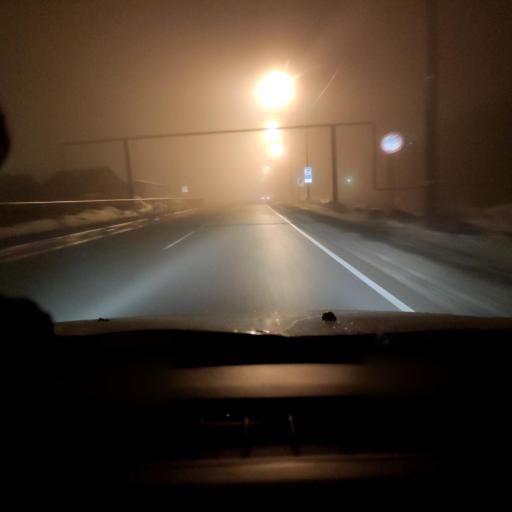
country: RU
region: Samara
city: Dubovyy Umet
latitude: 52.9620
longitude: 50.2905
